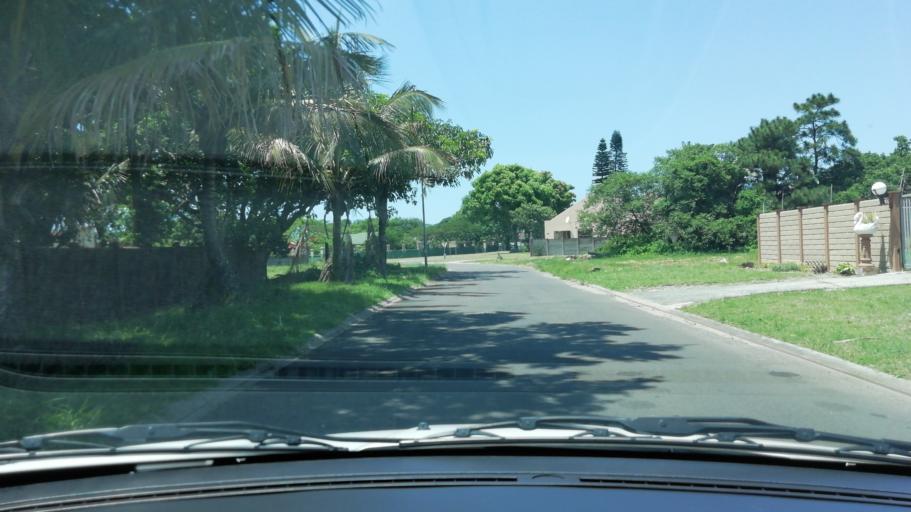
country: ZA
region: KwaZulu-Natal
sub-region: uThungulu District Municipality
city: Richards Bay
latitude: -28.7351
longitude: 32.0462
